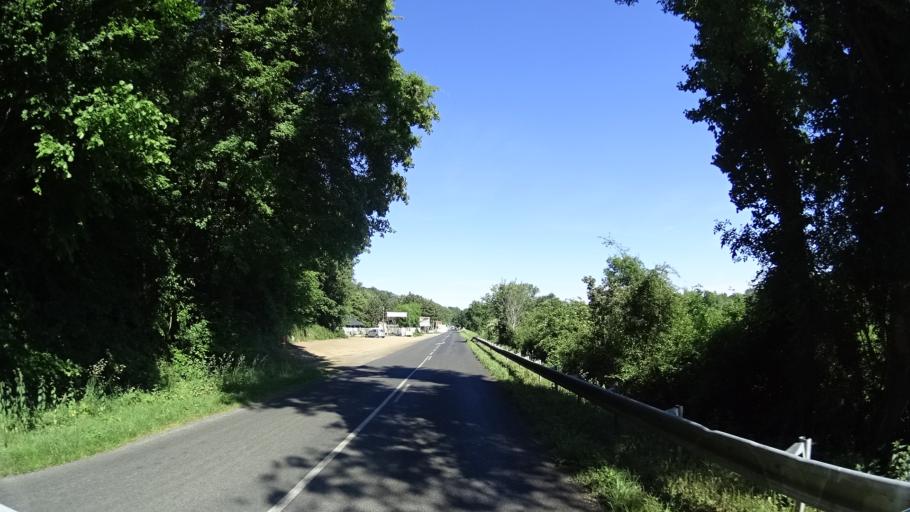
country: FR
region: Pays de la Loire
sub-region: Departement de Maine-et-Loire
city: Saint-Martin-de-la-Place
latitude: 47.2845
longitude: -0.1253
